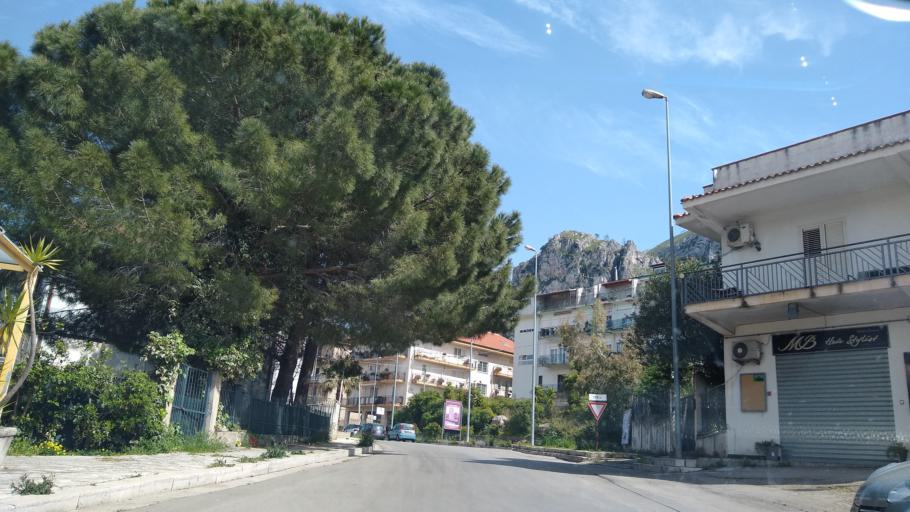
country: IT
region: Sicily
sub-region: Palermo
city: San Giuseppe Jato
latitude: 37.9749
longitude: 13.1942
